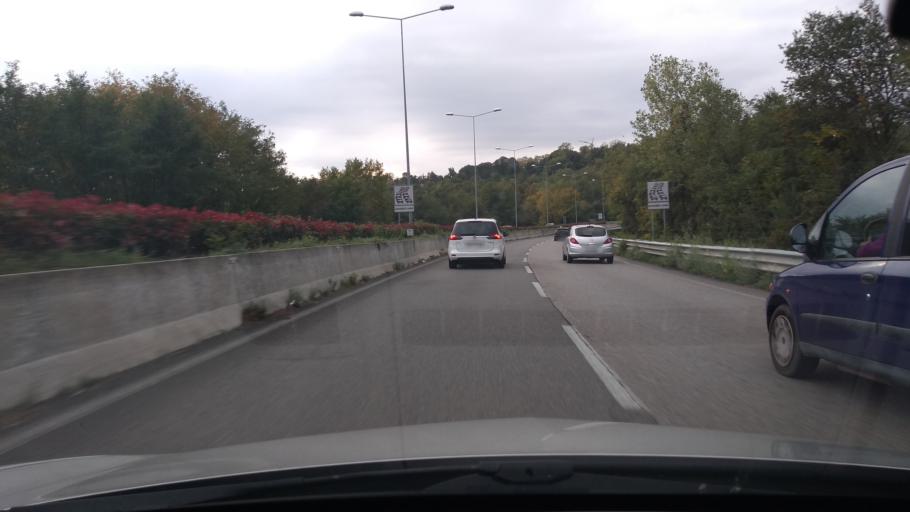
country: IT
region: Lombardy
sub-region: Provincia di Bergamo
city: Ghiaie
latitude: 45.6735
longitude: 9.5807
